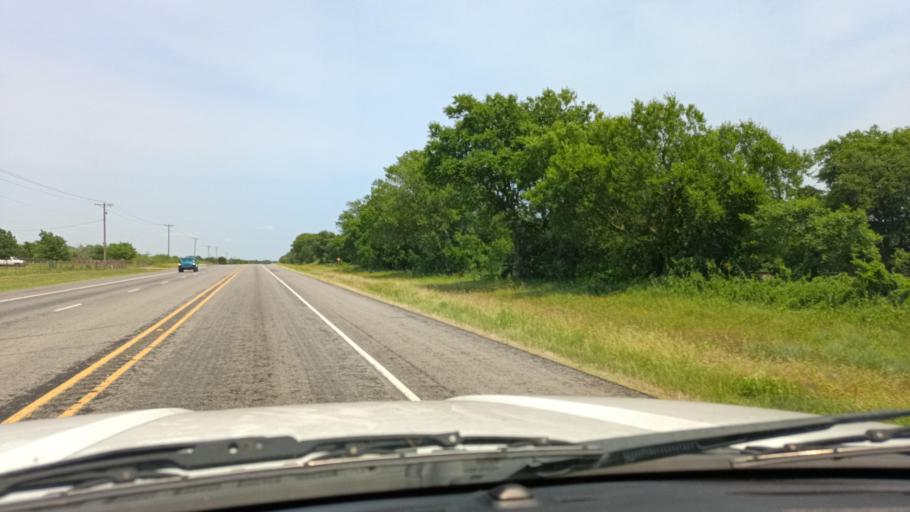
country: US
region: Texas
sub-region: Milam County
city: Cameron
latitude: 30.8489
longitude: -97.0429
